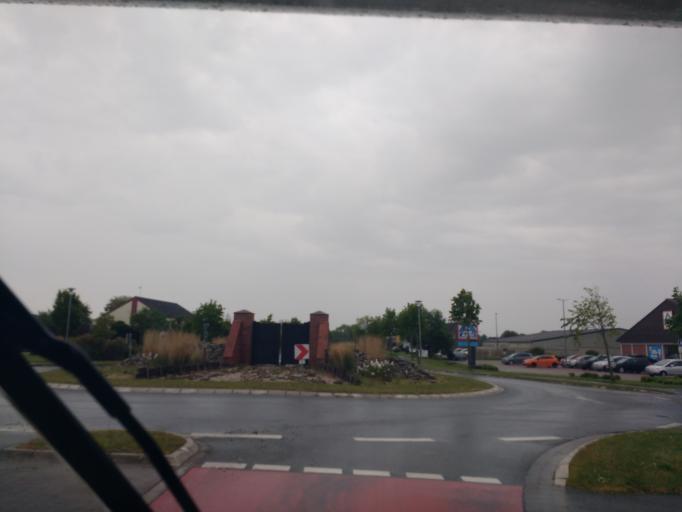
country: DE
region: Lower Saxony
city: Jever
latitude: 53.6677
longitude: 7.9112
